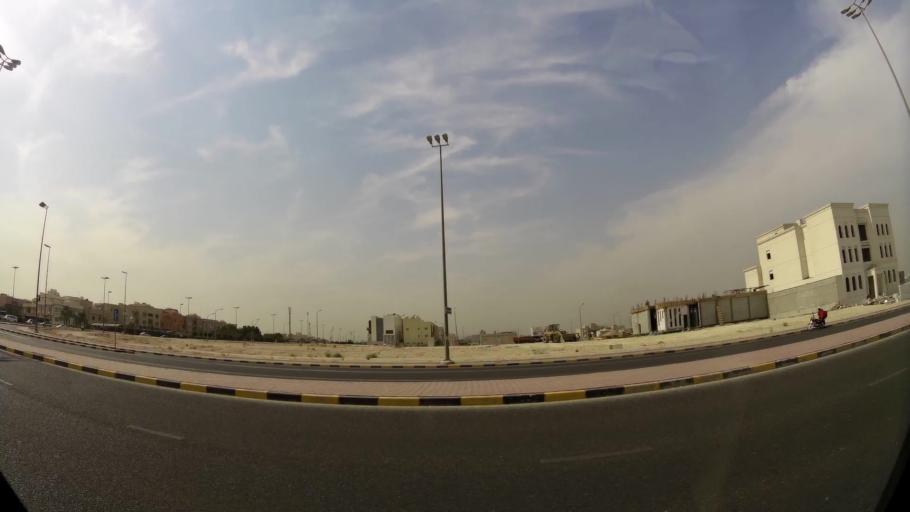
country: KW
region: Al Farwaniyah
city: Janub as Surrah
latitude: 29.2865
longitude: 47.9937
